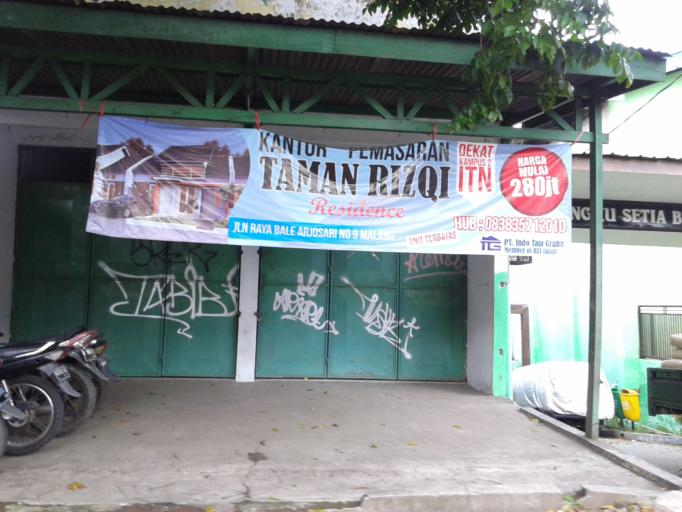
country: ID
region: East Java
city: Singosari
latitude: -7.9287
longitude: 112.6487
